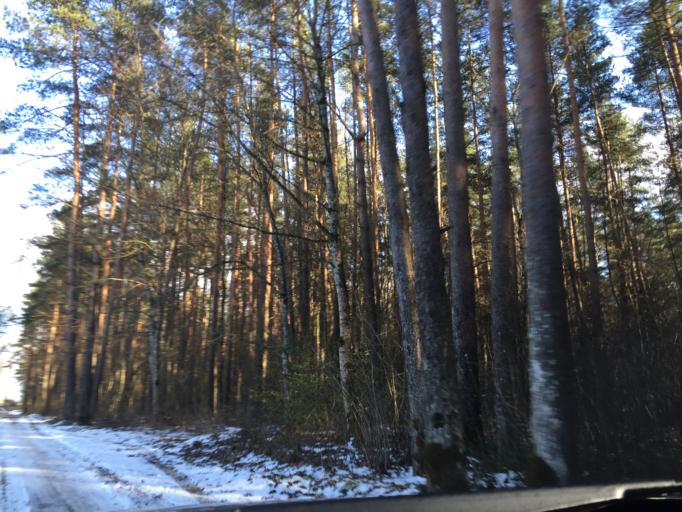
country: LV
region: Kekava
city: Kekava
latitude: 56.8476
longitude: 24.1848
